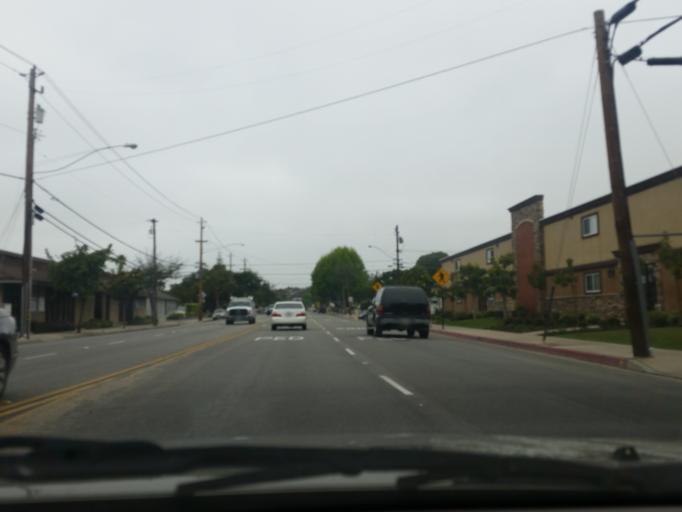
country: US
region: California
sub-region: San Luis Obispo County
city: Arroyo Grande
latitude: 35.1148
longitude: -120.5915
